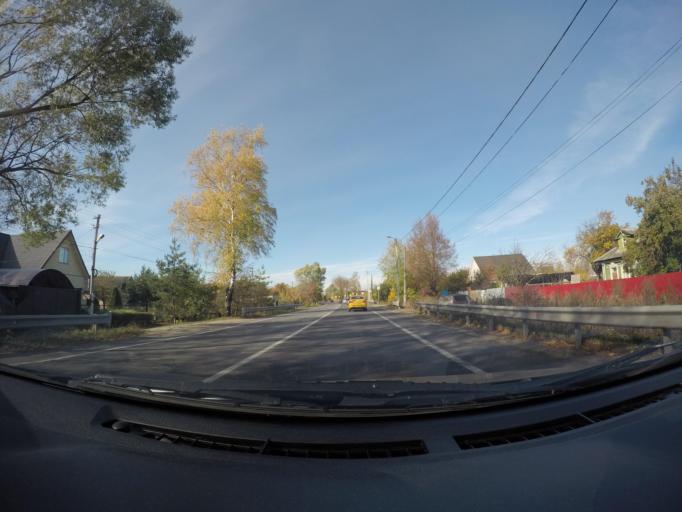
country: RU
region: Moskovskaya
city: Gzhel'
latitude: 55.6065
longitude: 38.4161
